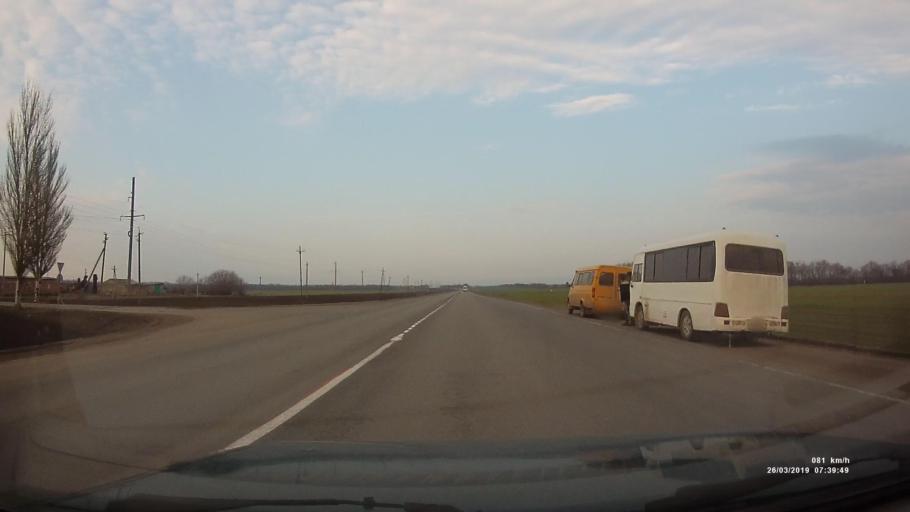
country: RU
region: Rostov
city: Novobessergenovka
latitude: 47.1962
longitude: 38.6587
